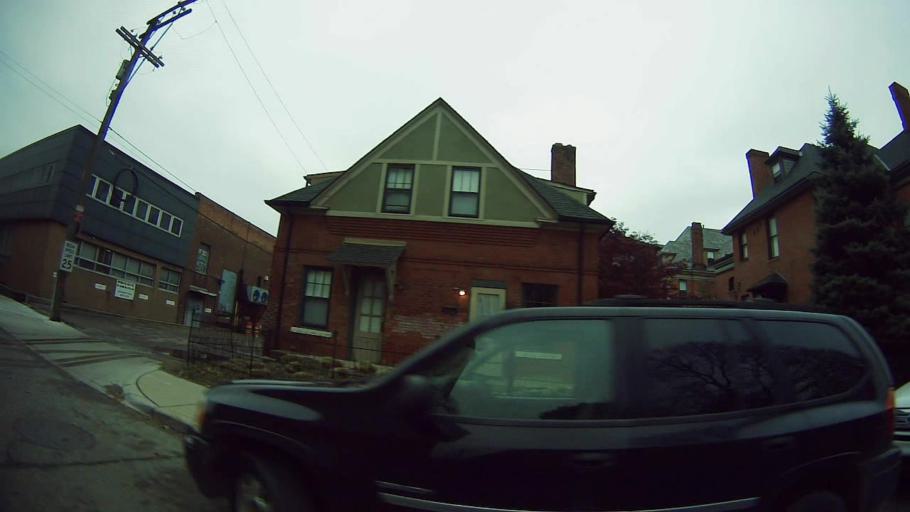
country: US
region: Michigan
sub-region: Wayne County
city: Hamtramck
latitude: 42.3615
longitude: -83.0647
